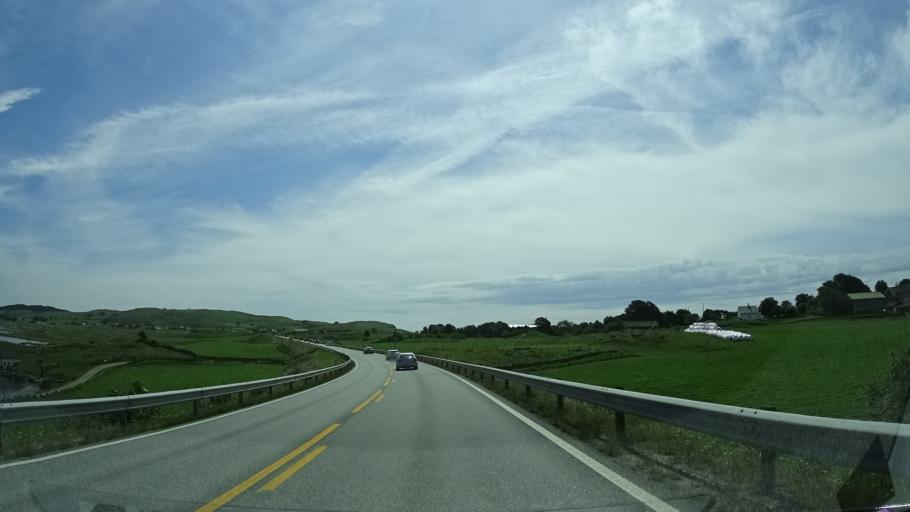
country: NO
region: Rogaland
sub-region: Rennesoy
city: Vikevag
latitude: 59.1348
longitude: 5.6045
